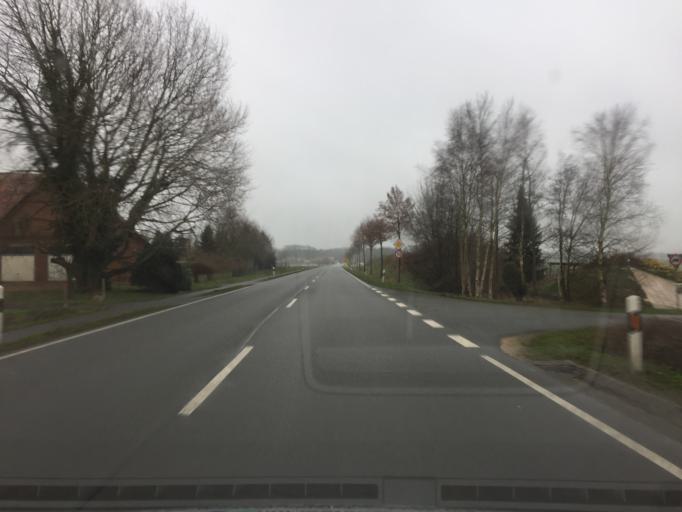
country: DE
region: Lower Saxony
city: Kirchdorf
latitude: 52.5690
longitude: 8.8491
